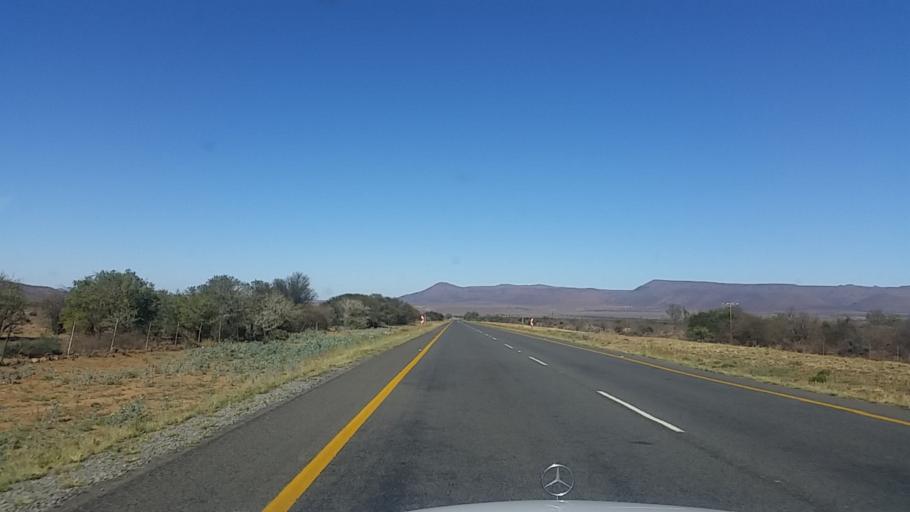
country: ZA
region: Eastern Cape
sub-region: Cacadu District Municipality
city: Graaff-Reinet
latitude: -31.9827
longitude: 24.6969
